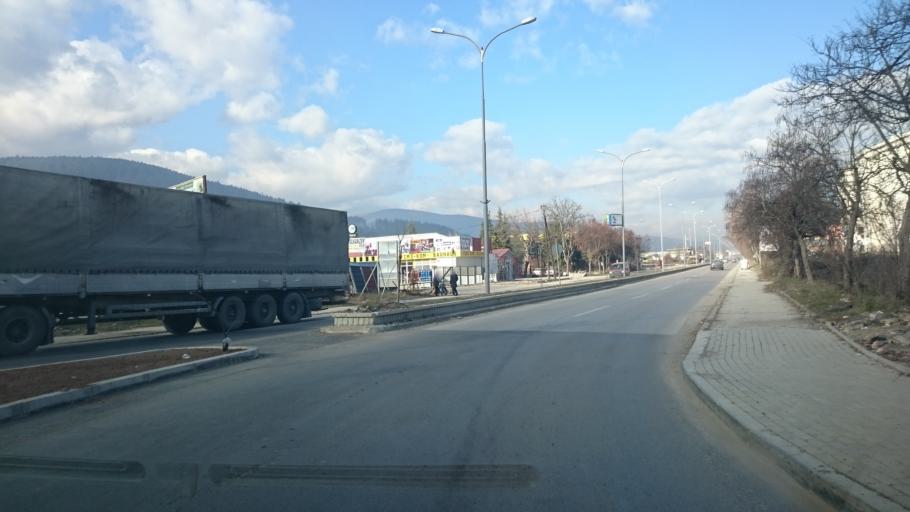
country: MK
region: Kicevo
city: Kicevo
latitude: 41.5067
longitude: 20.9525
